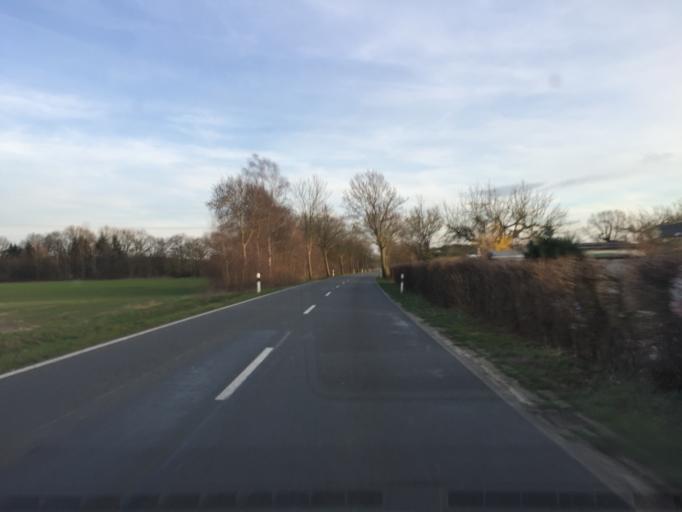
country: DE
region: Lower Saxony
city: Neustadt am Rubenberge
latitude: 52.4998
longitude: 9.4841
